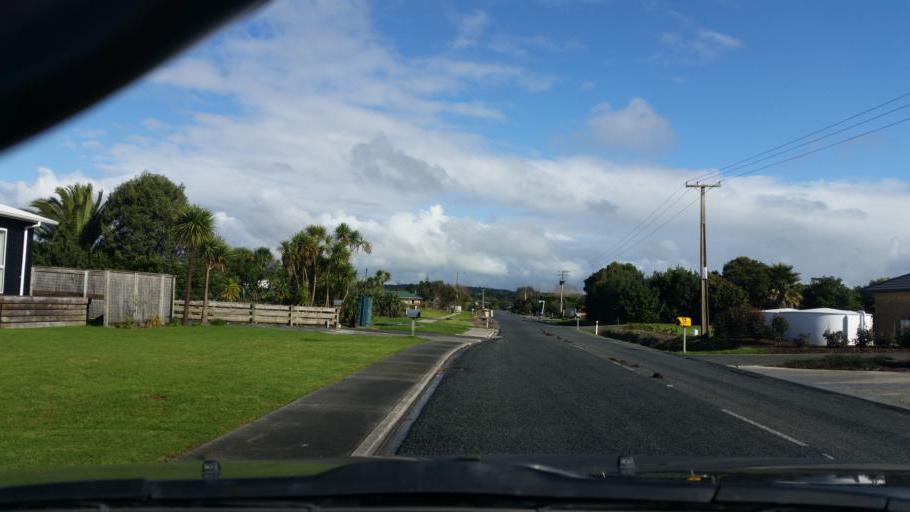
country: NZ
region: Auckland
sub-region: Auckland
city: Wellsford
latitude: -36.0883
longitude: 174.5750
